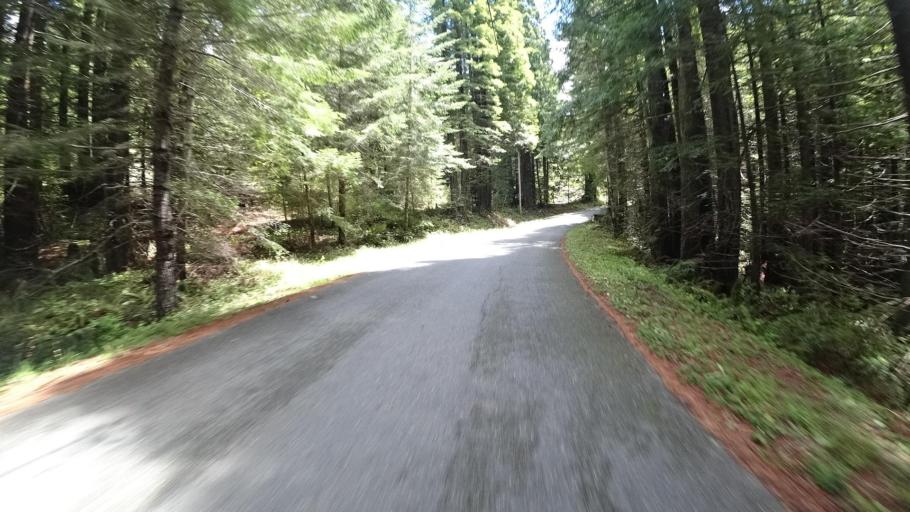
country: US
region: California
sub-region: Humboldt County
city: Blue Lake
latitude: 40.8466
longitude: -123.9247
